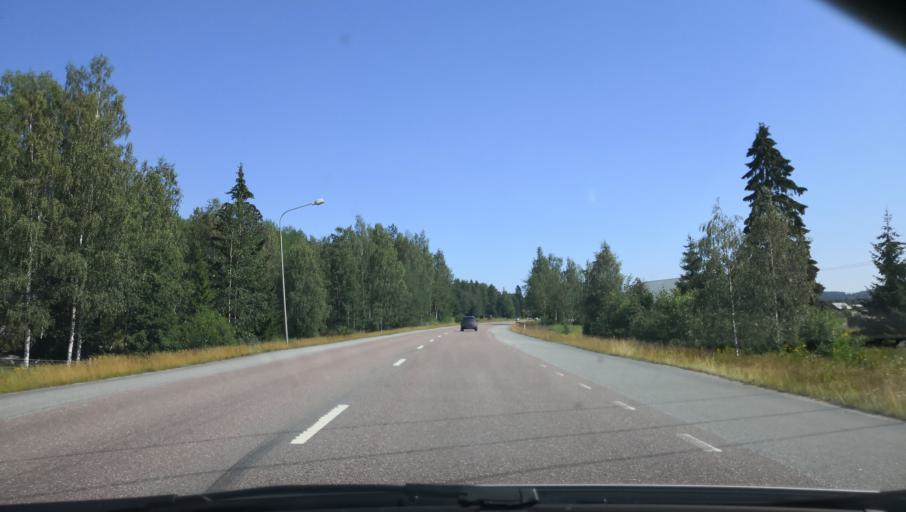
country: SE
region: Gaevleborg
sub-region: Ovanakers Kommun
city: Alfta
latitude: 61.3343
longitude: 16.2210
